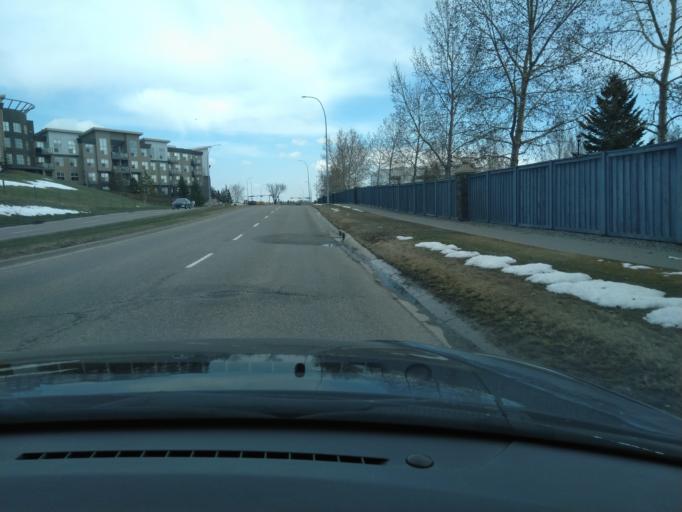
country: CA
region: Alberta
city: Calgary
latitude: 51.1279
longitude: -114.2126
